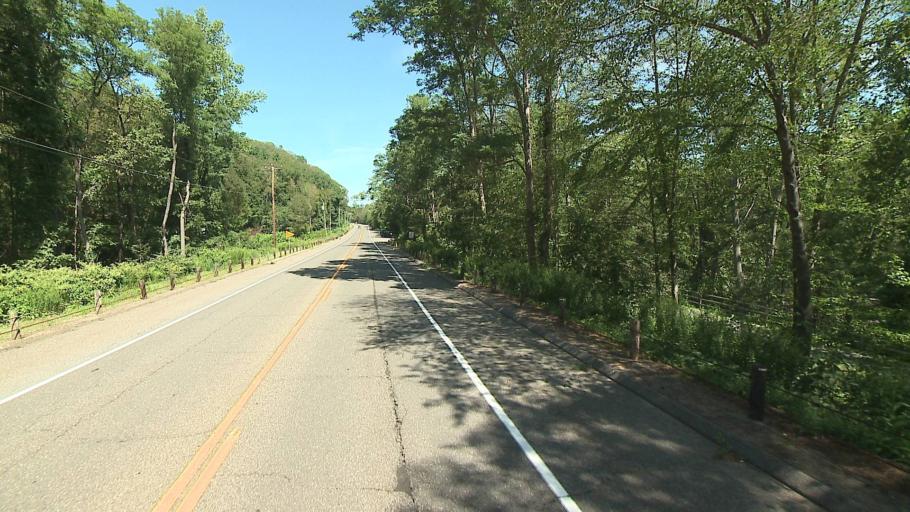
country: US
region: Connecticut
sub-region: Hartford County
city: Collinsville
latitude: 41.7927
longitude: -72.9252
